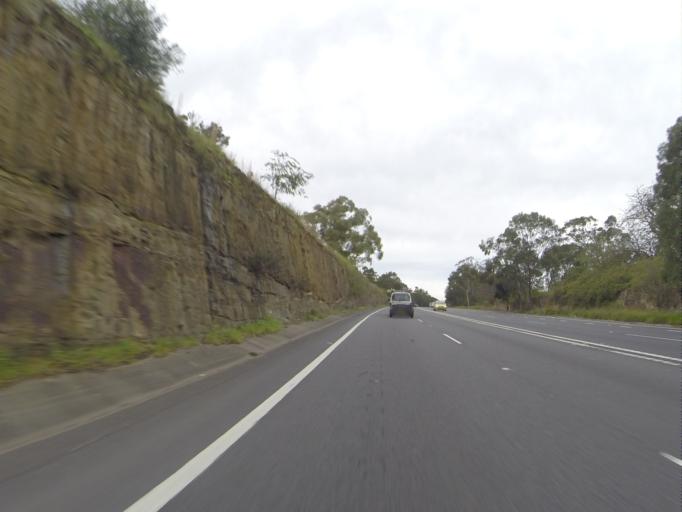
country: AU
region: New South Wales
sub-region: Sutherland Shire
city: Menai
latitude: -34.0060
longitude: 151.0139
